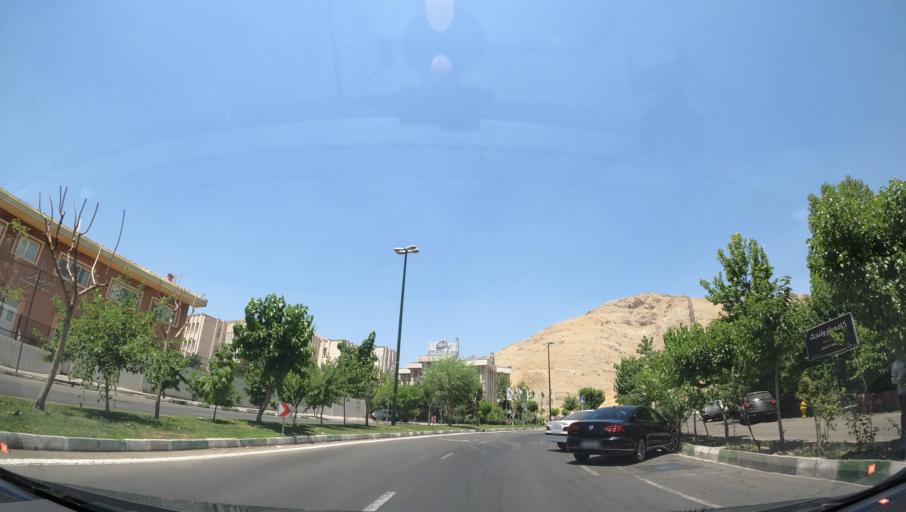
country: IR
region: Tehran
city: Tajrish
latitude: 35.8089
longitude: 51.3896
